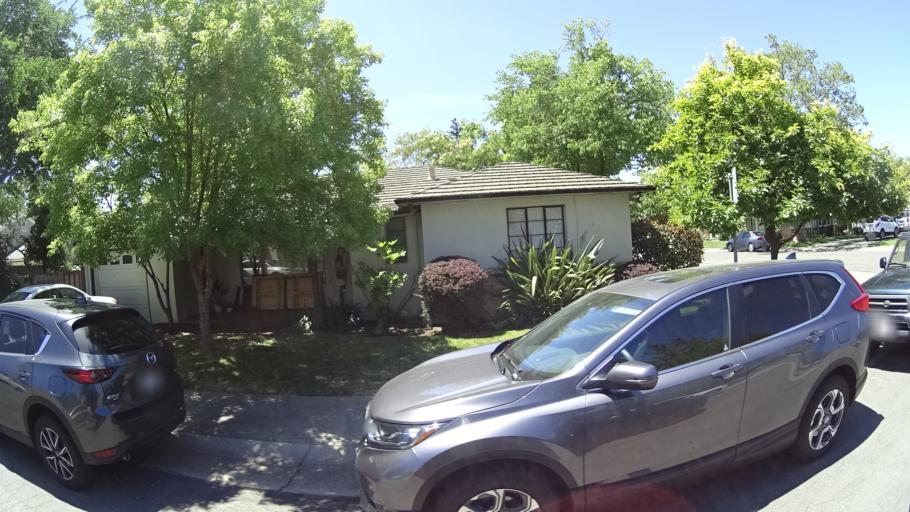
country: US
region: California
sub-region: Sacramento County
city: Sacramento
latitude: 38.5716
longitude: -121.4357
